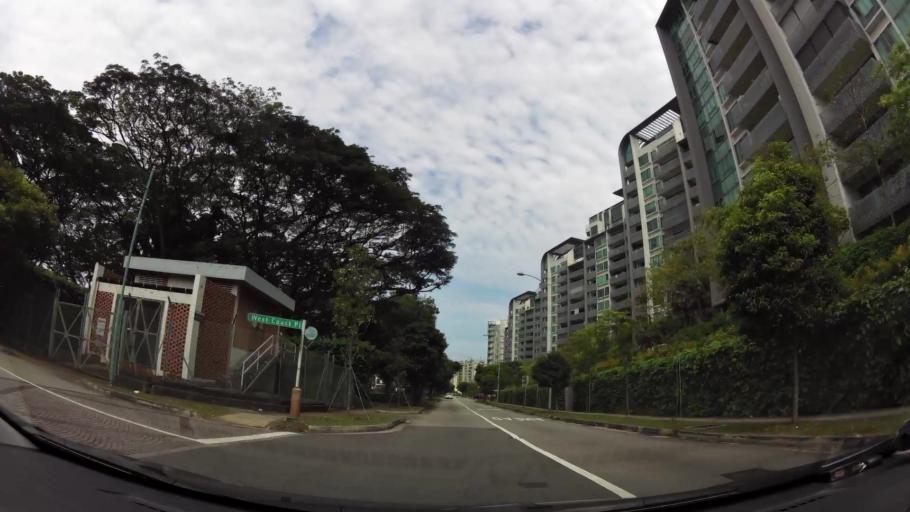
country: SG
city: Singapore
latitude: 1.3138
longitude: 103.7593
